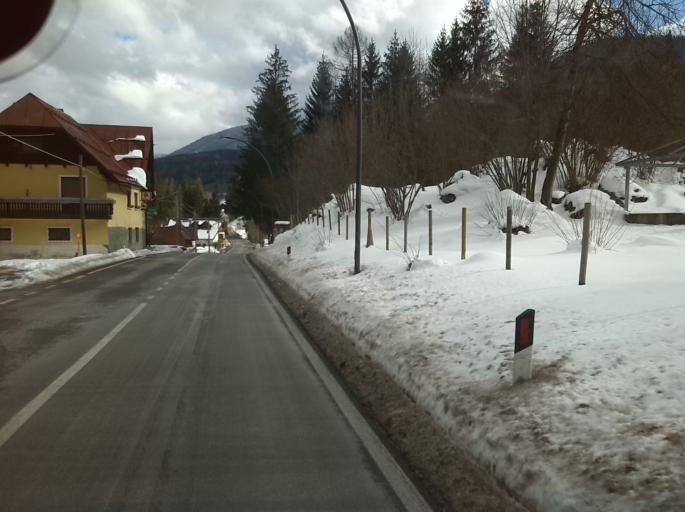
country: IT
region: Friuli Venezia Giulia
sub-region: Provincia di Udine
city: Tarvisio
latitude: 46.4974
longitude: 13.6323
